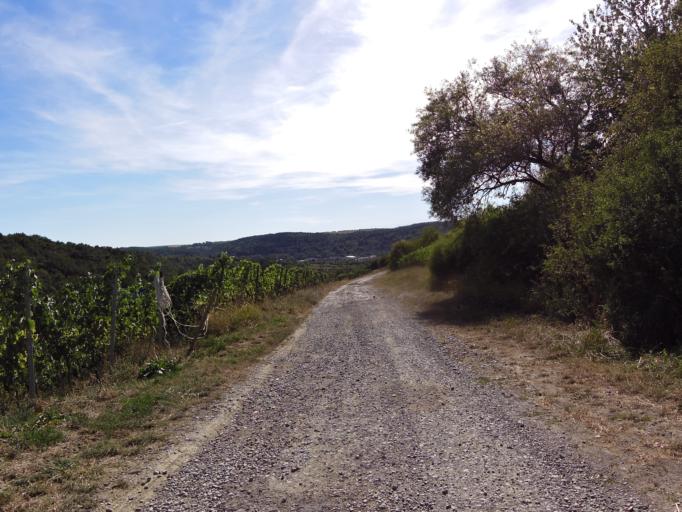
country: DE
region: Bavaria
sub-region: Regierungsbezirk Unterfranken
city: Eibelstadt
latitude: 49.7414
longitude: 10.0070
